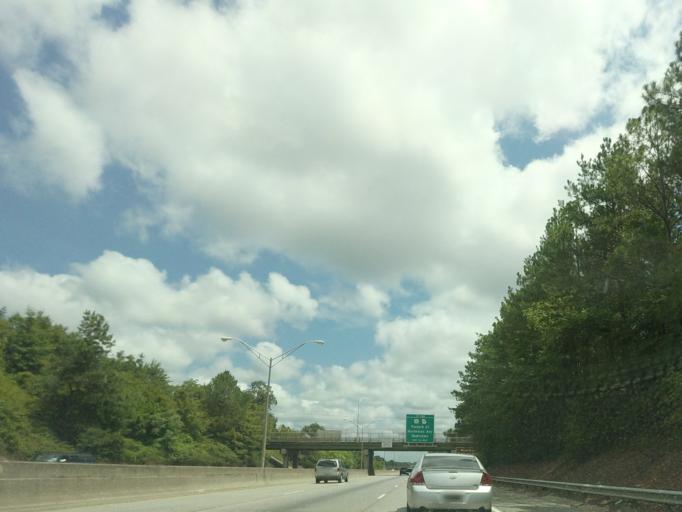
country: US
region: Georgia
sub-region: Bibb County
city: Macon
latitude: 32.8330
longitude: -83.6525
